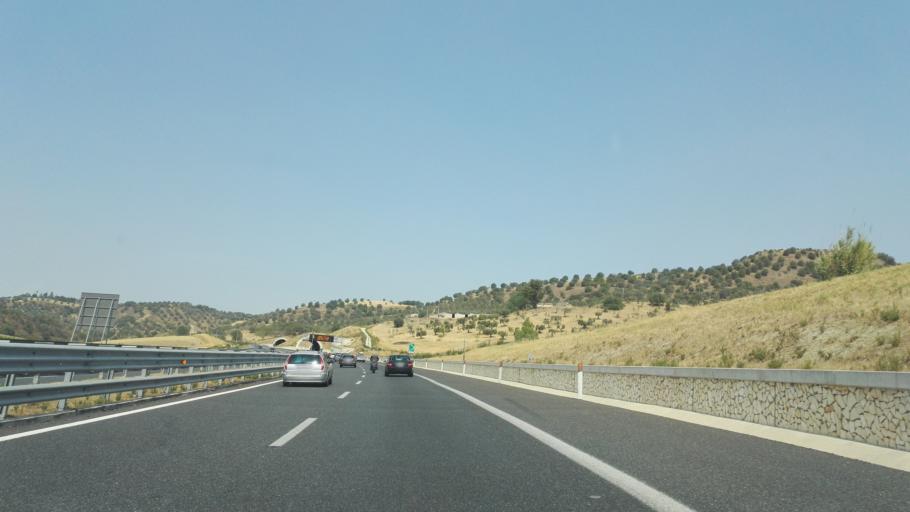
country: IT
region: Calabria
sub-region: Provincia di Cosenza
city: Tarsia
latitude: 39.5976
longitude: 16.2427
